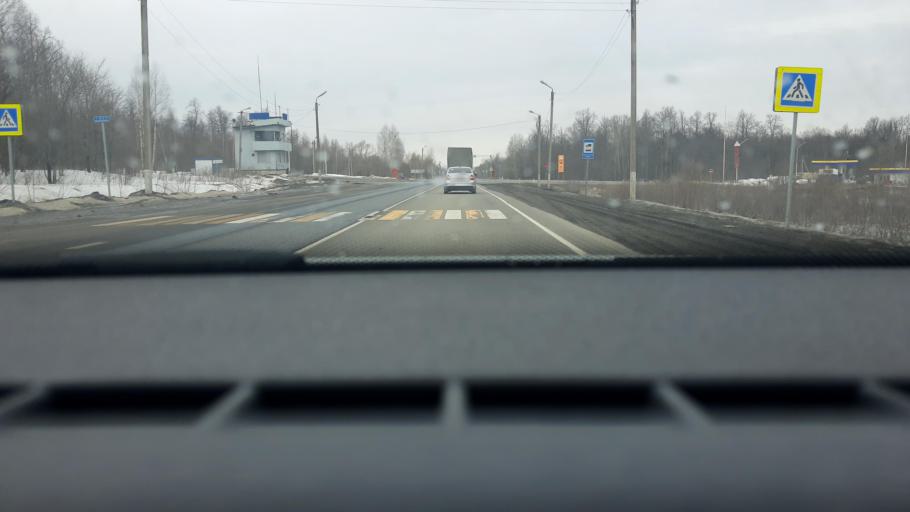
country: RU
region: Bashkortostan
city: Ulu-Telyak
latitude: 54.8420
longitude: 57.0610
